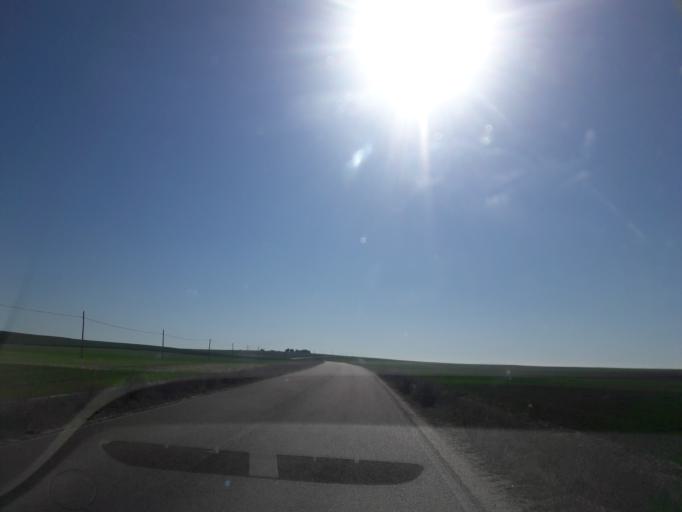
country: ES
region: Castille and Leon
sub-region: Provincia de Salamanca
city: Tordillos
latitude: 40.8499
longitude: -5.3243
